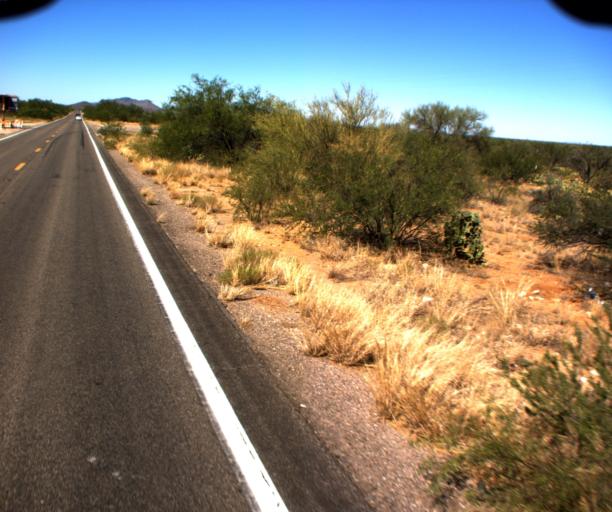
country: US
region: Arizona
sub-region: Pima County
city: Sells
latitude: 31.9599
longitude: -111.7526
